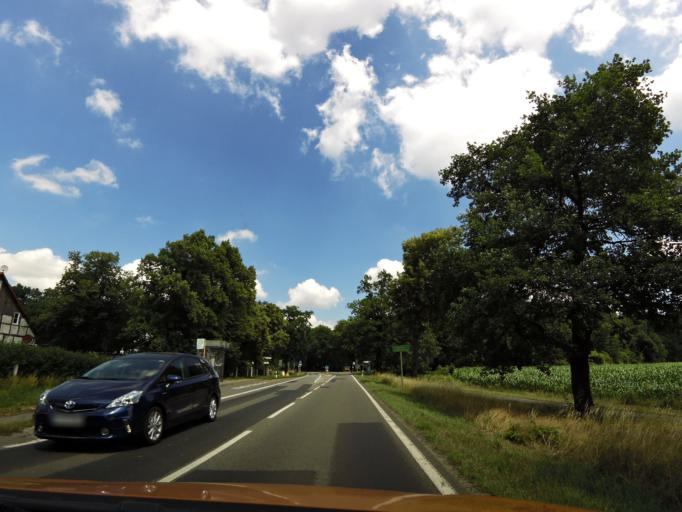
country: DE
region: Brandenburg
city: Nauen
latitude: 52.6300
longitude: 12.9031
